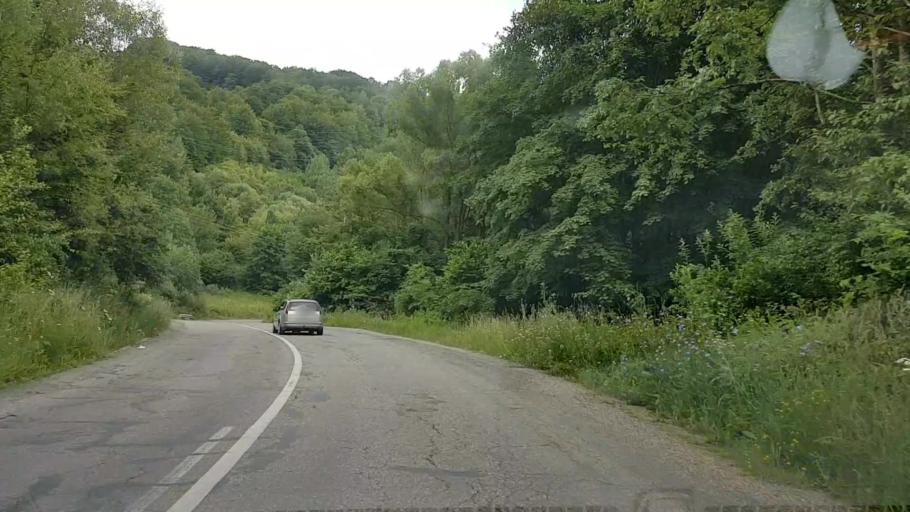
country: RO
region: Neamt
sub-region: Comuna Pangarati
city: Pangarati
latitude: 46.9484
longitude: 26.1301
